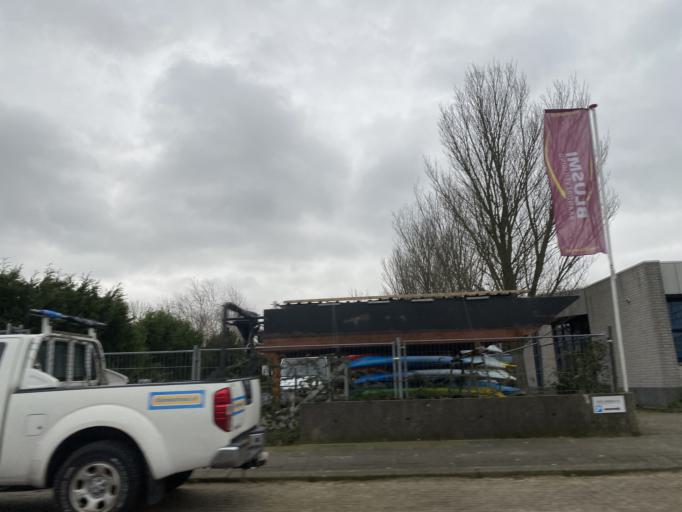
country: NL
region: North Holland
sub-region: Gemeente Zaanstad
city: Zaanstad
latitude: 52.4895
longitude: 4.8126
